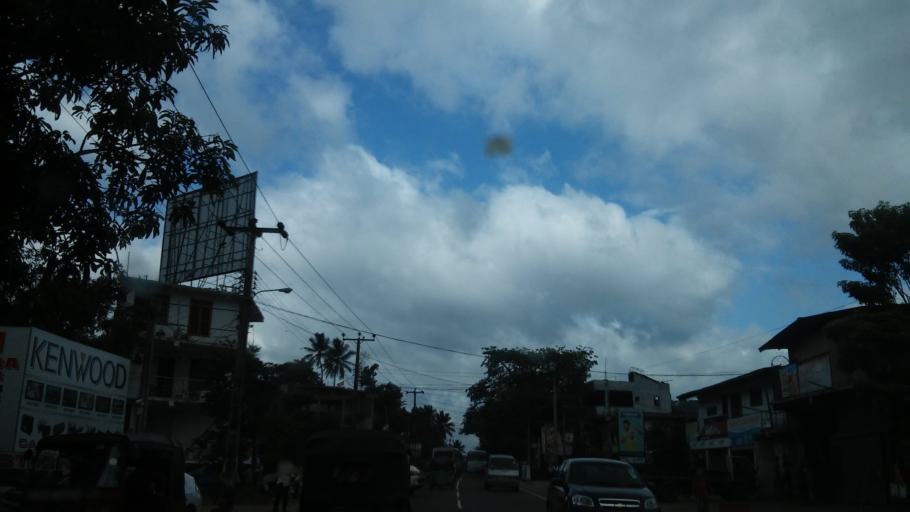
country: LK
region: Central
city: Kandy
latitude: 7.2846
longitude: 80.6270
